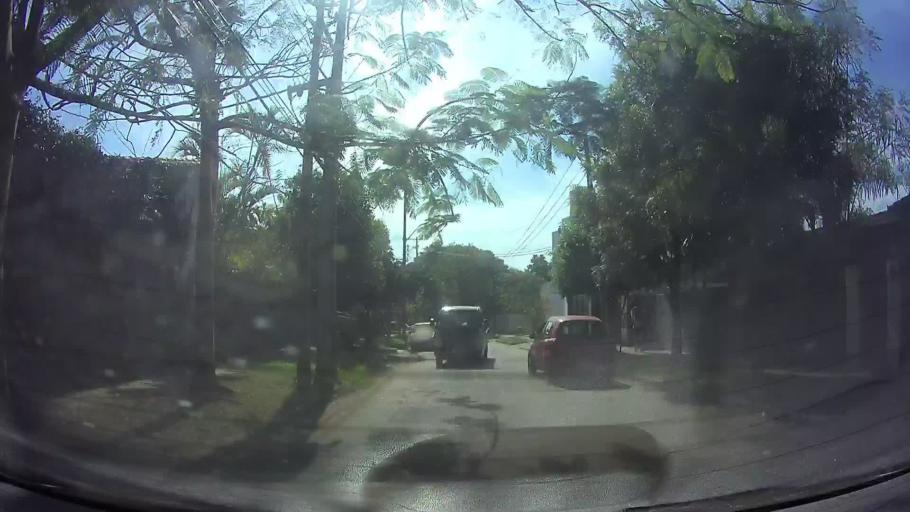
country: PY
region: Central
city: Fernando de la Mora
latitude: -25.2824
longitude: -57.5447
